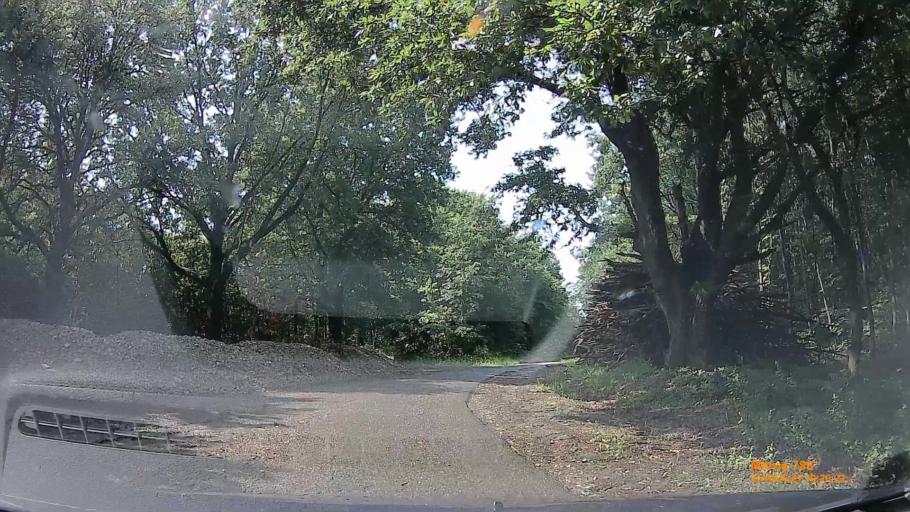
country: HU
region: Baranya
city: Buekkoesd
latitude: 46.1773
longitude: 17.9761
